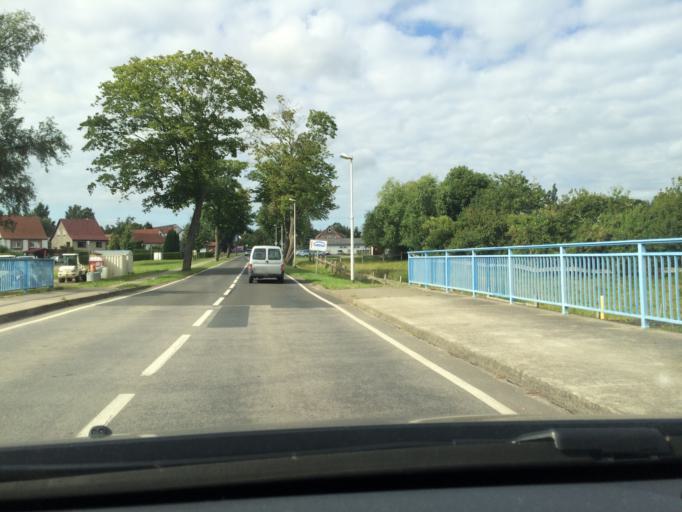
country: DE
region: Mecklenburg-Vorpommern
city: Prohn
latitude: 54.3708
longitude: 13.0235
